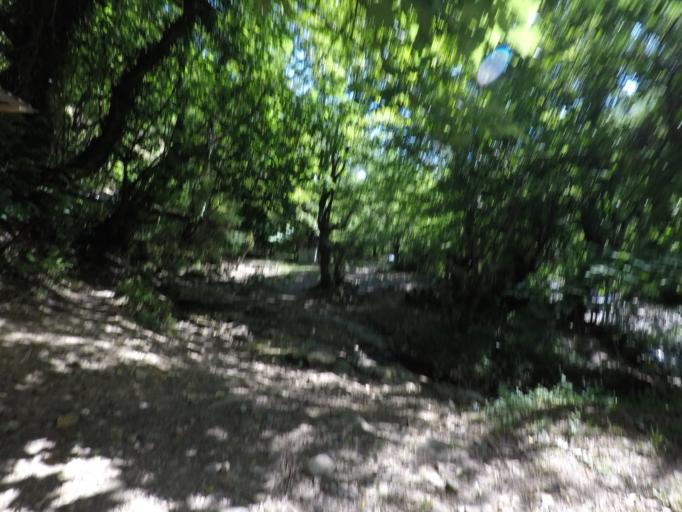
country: AZ
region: Qakh Rayon
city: Cinarli
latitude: 41.4891
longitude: 46.8560
